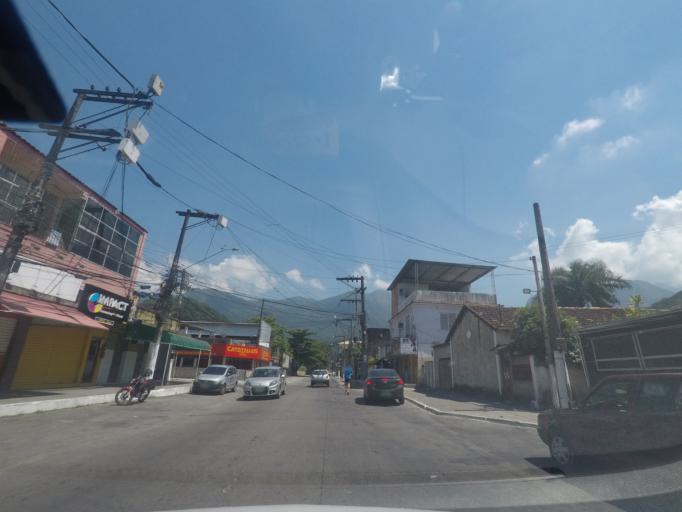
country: BR
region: Rio de Janeiro
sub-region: Petropolis
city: Petropolis
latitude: -22.5867
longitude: -43.1859
